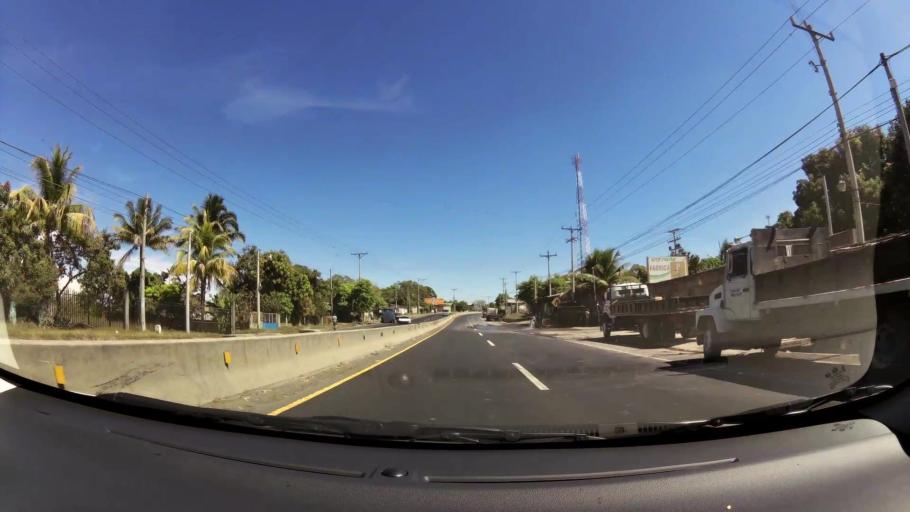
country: SV
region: La Libertad
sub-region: Distrito de Quezaltepeque
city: Quezaltepeque
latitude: 13.8158
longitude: -89.3111
